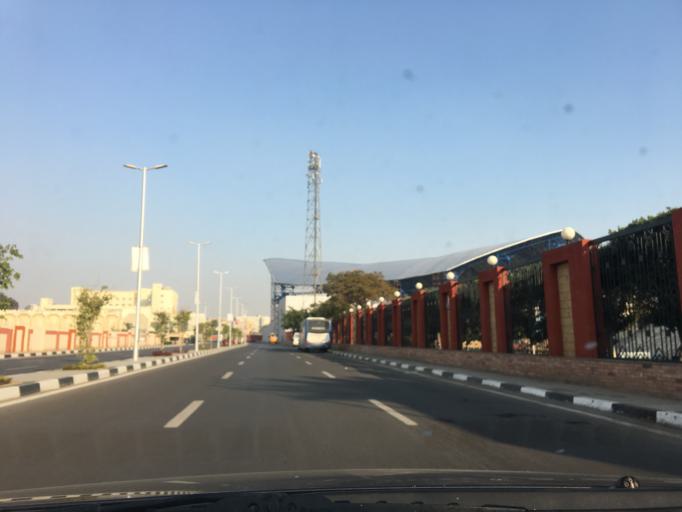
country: EG
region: Muhafazat al Qahirah
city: Cairo
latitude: 30.0718
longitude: 31.3054
